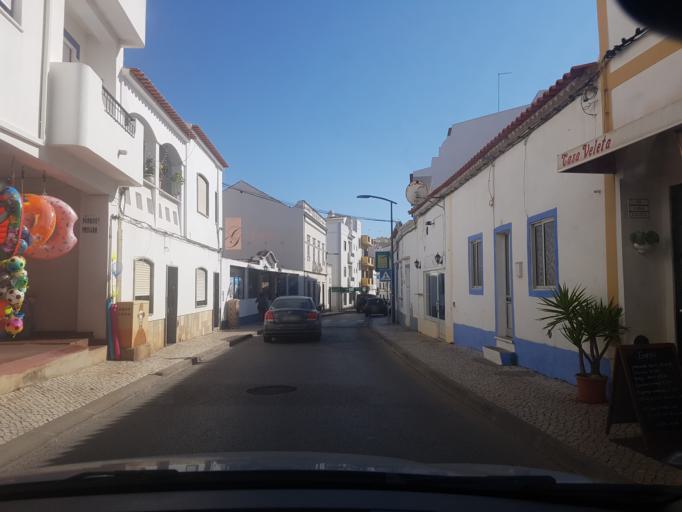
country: PT
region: Faro
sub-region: Lagoa
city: Carvoeiro
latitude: 37.0991
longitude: -8.4700
